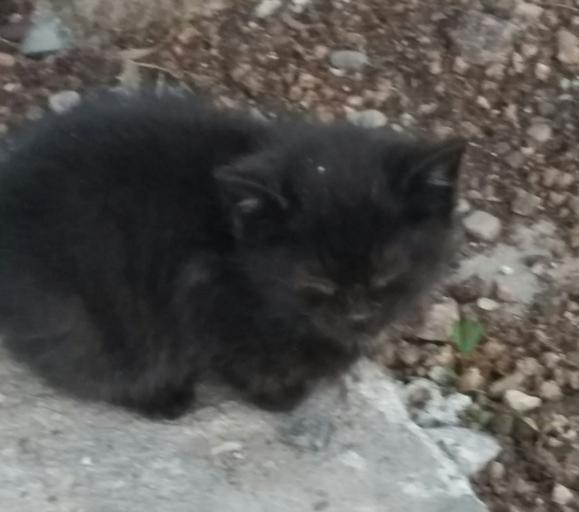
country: US
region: Ohio
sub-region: Holmes County
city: Millersburg
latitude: 40.4535
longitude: -81.8591
